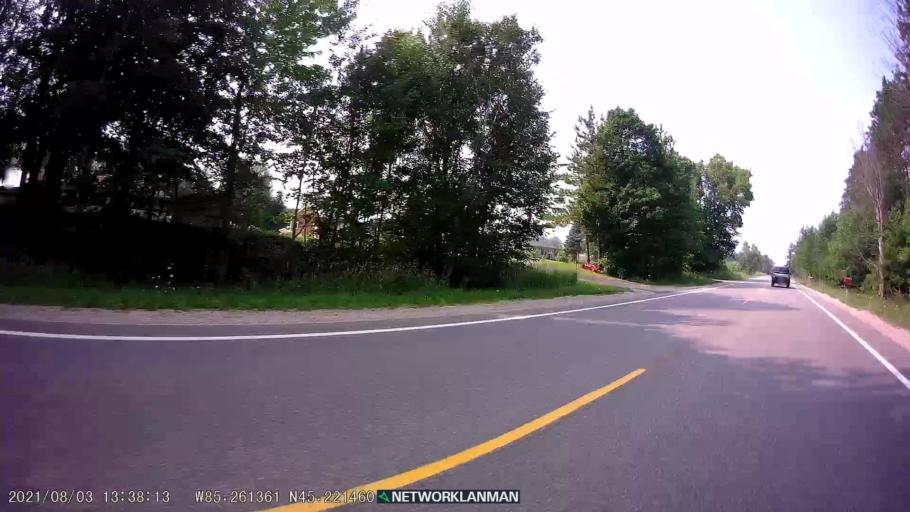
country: US
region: Michigan
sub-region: Charlevoix County
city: Charlevoix
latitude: 45.2218
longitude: -85.2613
